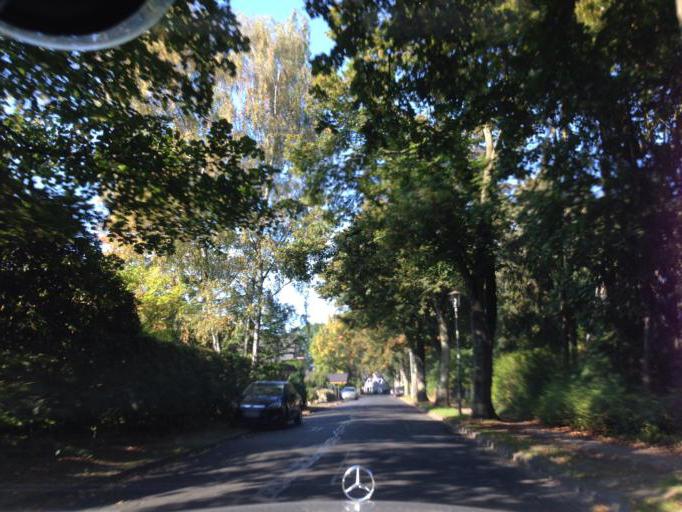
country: DE
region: Schleswig-Holstein
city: Ahrensburg
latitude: 53.6758
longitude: 10.2129
